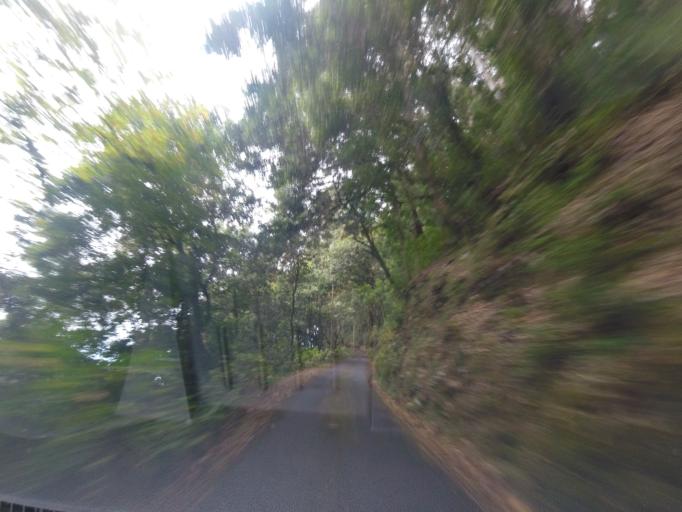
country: PT
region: Madeira
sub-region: Santana
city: Santana
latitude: 32.7850
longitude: -16.8990
